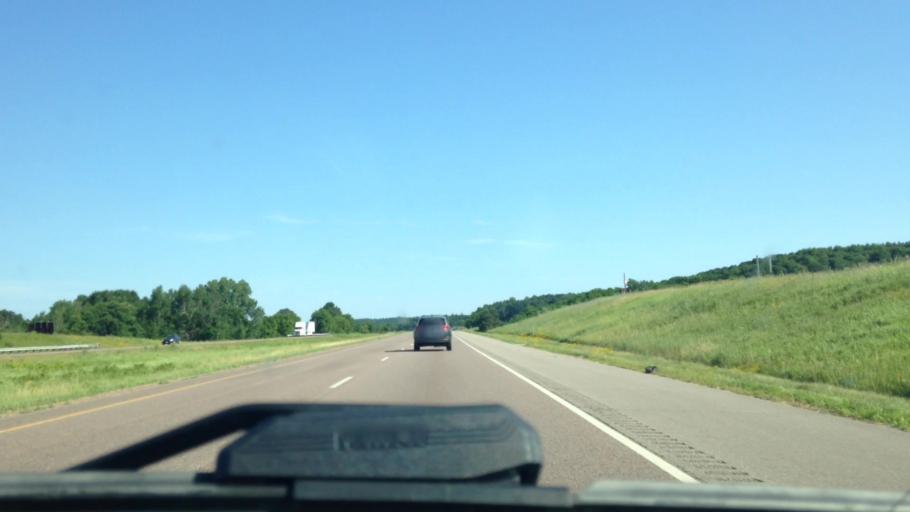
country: US
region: Wisconsin
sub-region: Eau Claire County
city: Fall Creek
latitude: 44.7075
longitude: -91.3444
